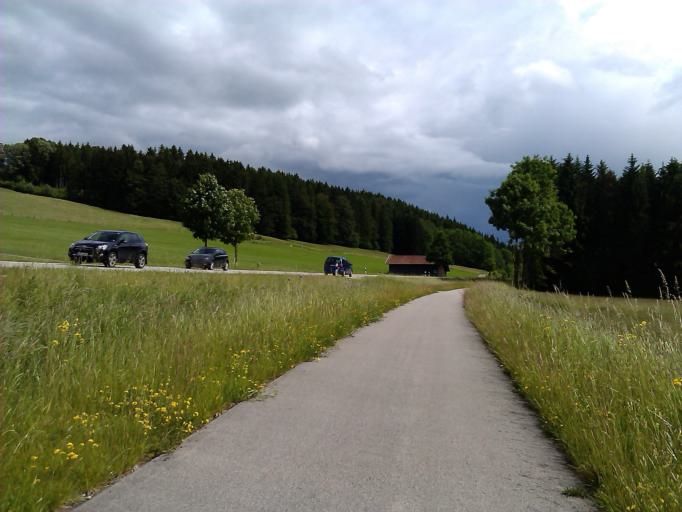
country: DE
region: Bavaria
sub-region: Swabia
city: Stotten am Auerberg
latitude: 47.7297
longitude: 10.6806
